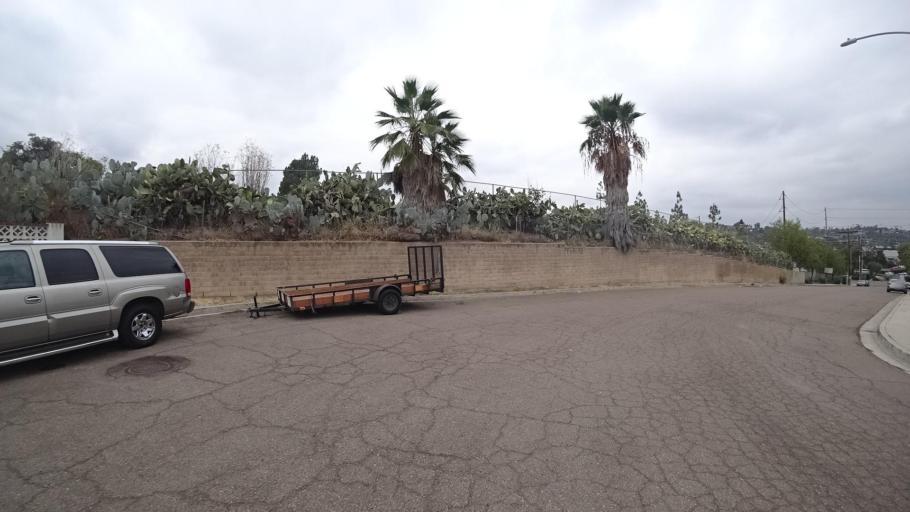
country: US
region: California
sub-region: San Diego County
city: Spring Valley
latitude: 32.7382
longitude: -117.0024
